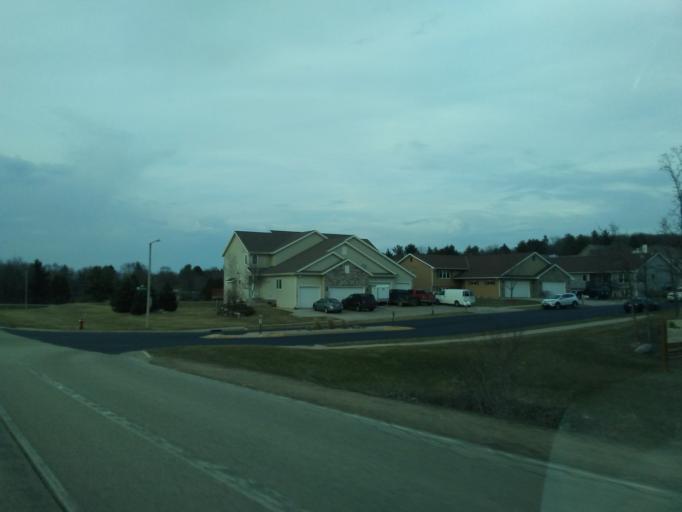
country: US
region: Wisconsin
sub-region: Dane County
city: Verona
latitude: 43.0080
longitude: -89.5336
